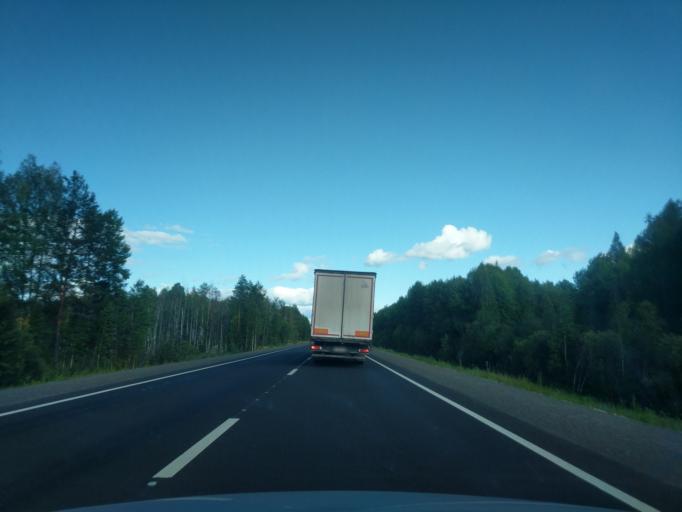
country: RU
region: Kostroma
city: Makar'yev
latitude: 57.8481
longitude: 43.6692
